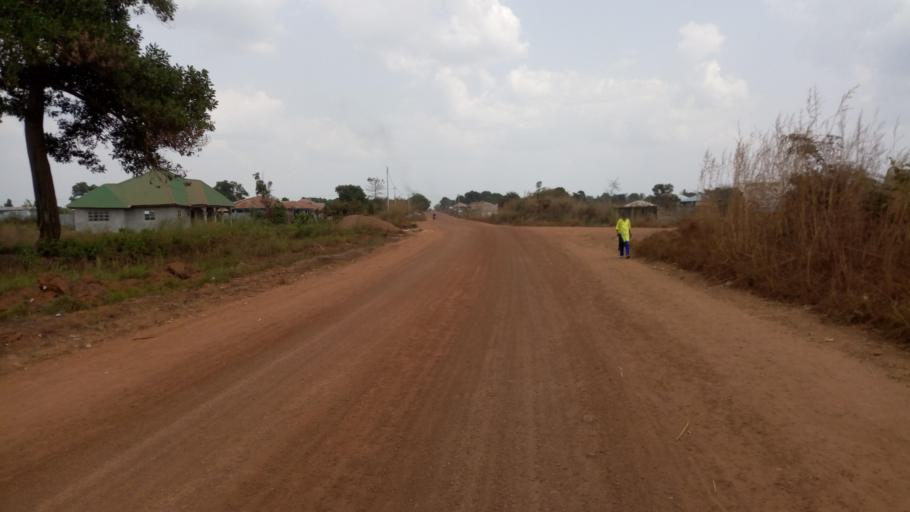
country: SL
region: Southern Province
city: Mogbwemo
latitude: 7.7863
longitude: -12.3114
